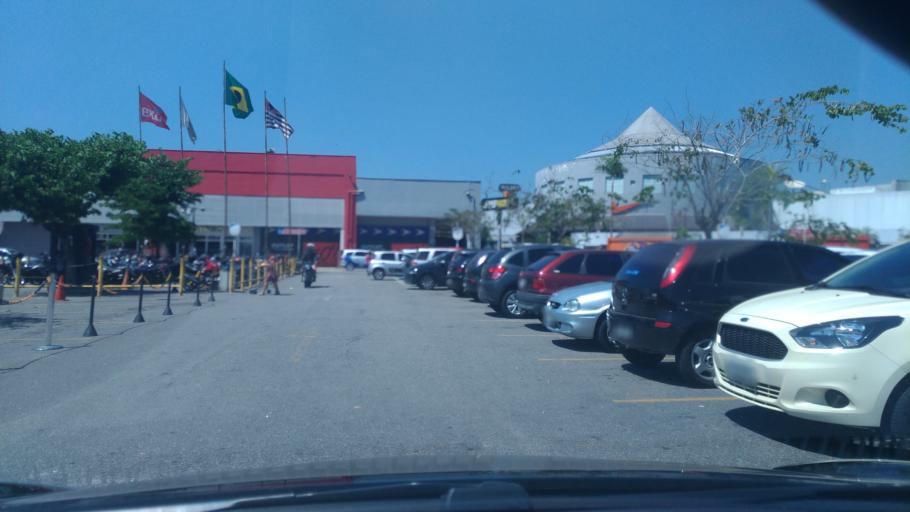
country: BR
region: Sao Paulo
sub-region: Sao Bernardo Do Campo
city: Sao Bernardo do Campo
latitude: -23.6682
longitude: -46.5749
